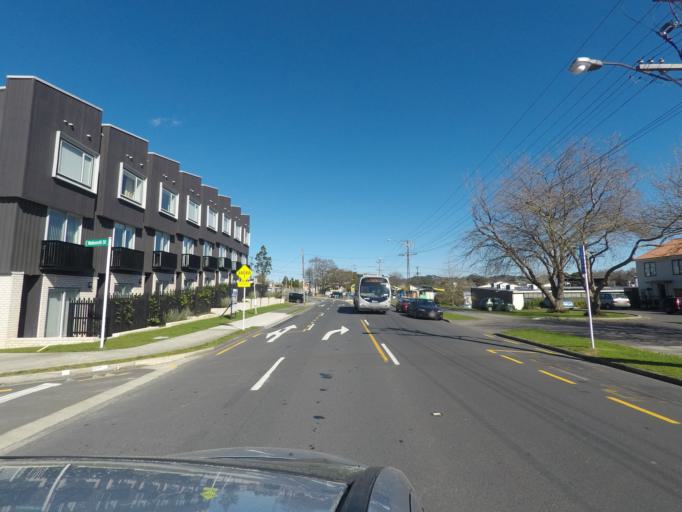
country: NZ
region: Auckland
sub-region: Auckland
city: Waitakere
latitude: -36.9128
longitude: 174.6818
